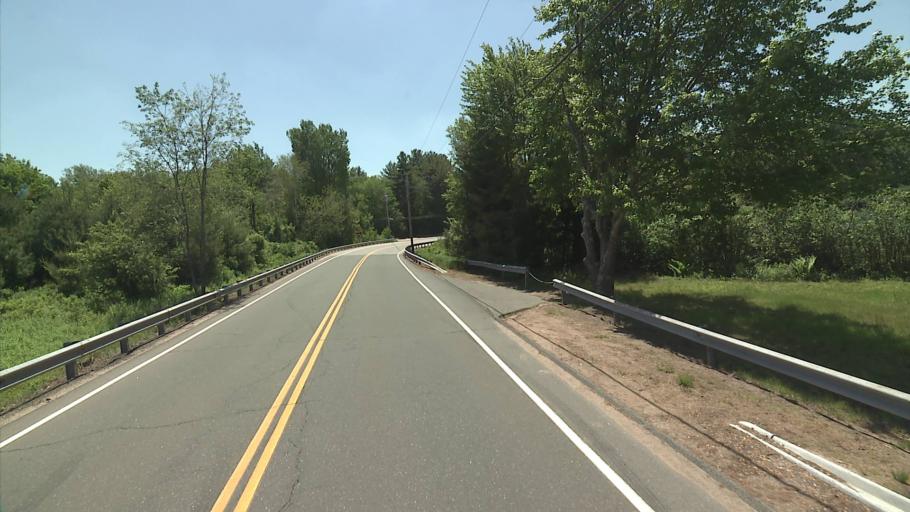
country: US
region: Connecticut
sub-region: Tolland County
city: Stafford
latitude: 41.9948
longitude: -72.2553
